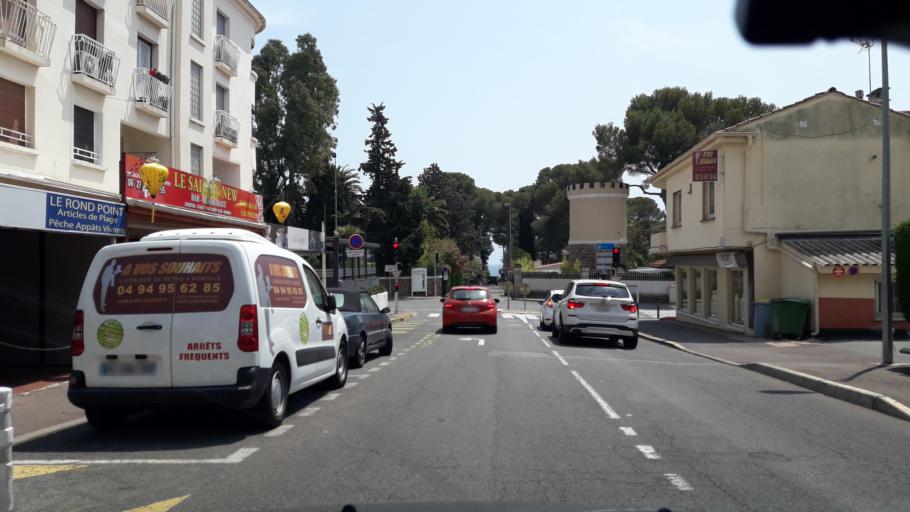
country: FR
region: Provence-Alpes-Cote d'Azur
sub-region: Departement du Var
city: Saint-Raphael
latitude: 43.4153
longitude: 6.8091
